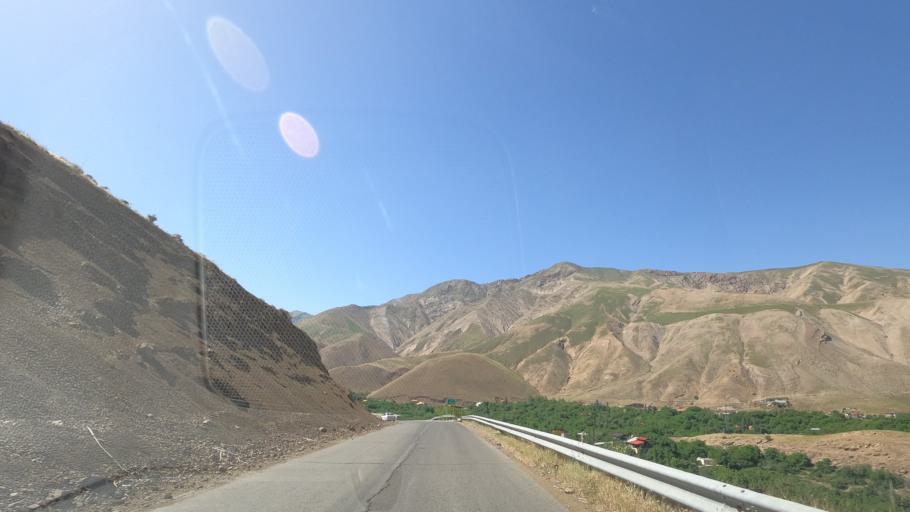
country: IR
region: Alborz
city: Karaj
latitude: 35.9274
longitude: 51.0872
